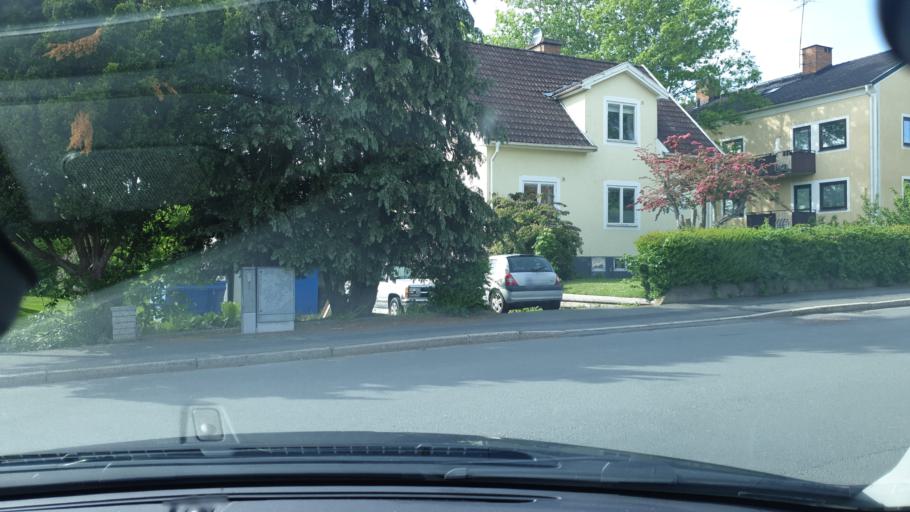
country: SE
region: Joenkoeping
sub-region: Vetlanda Kommun
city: Vetlanda
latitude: 57.4235
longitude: 15.0967
